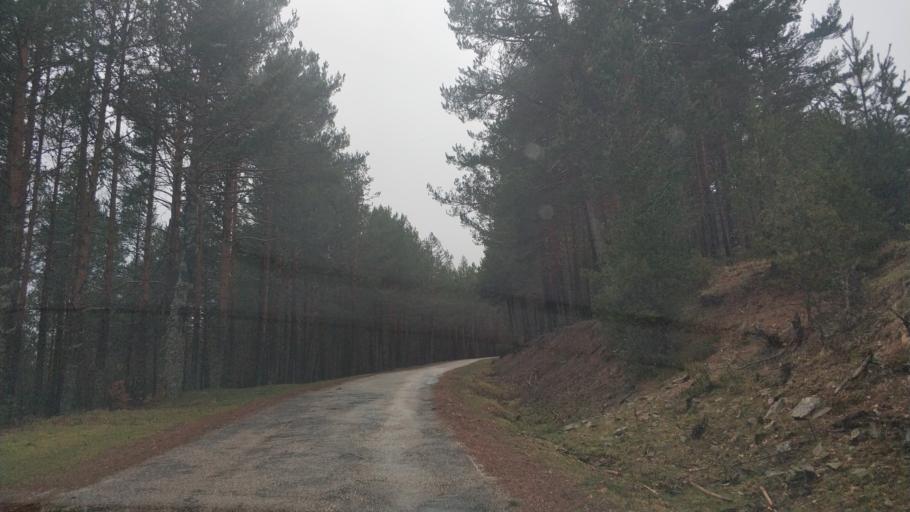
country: ES
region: Castille and Leon
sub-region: Provincia de Burgos
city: Neila
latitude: 42.0442
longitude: -3.0136
